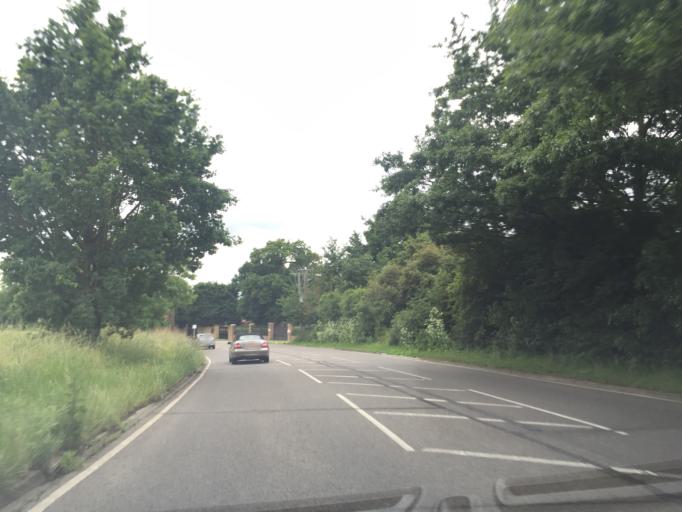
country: GB
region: England
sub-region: Essex
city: Theydon Bois
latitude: 51.6625
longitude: 0.1145
